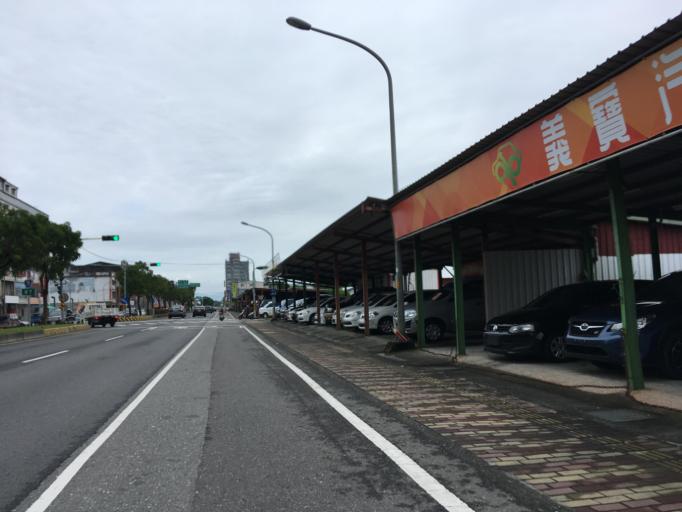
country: TW
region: Taiwan
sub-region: Yilan
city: Yilan
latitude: 24.7033
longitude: 121.7704
